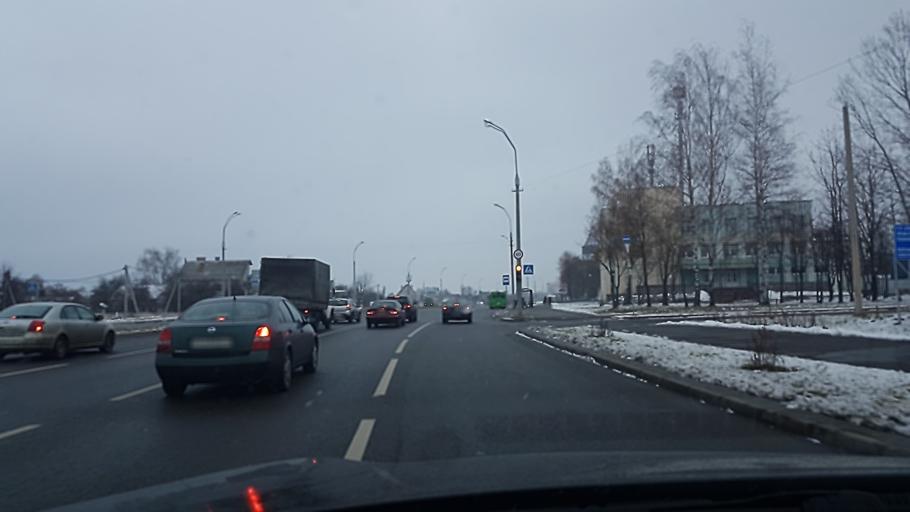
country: BY
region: Minsk
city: Bal'shavik
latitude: 53.9523
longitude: 27.5352
